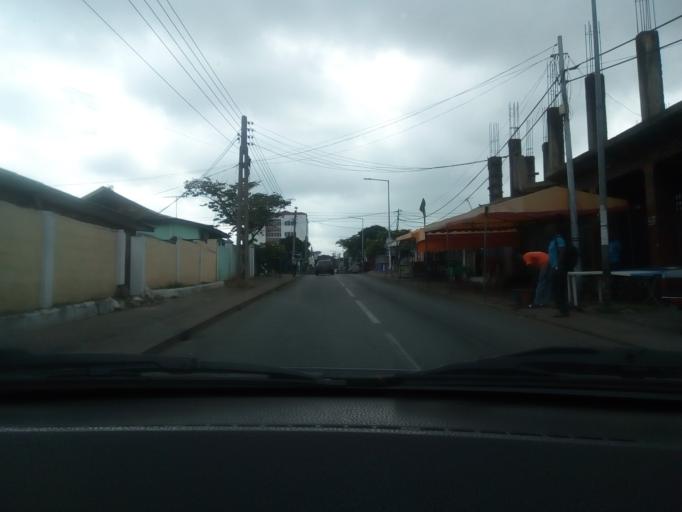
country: GH
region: Greater Accra
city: Accra
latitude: 5.5596
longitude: -0.2123
